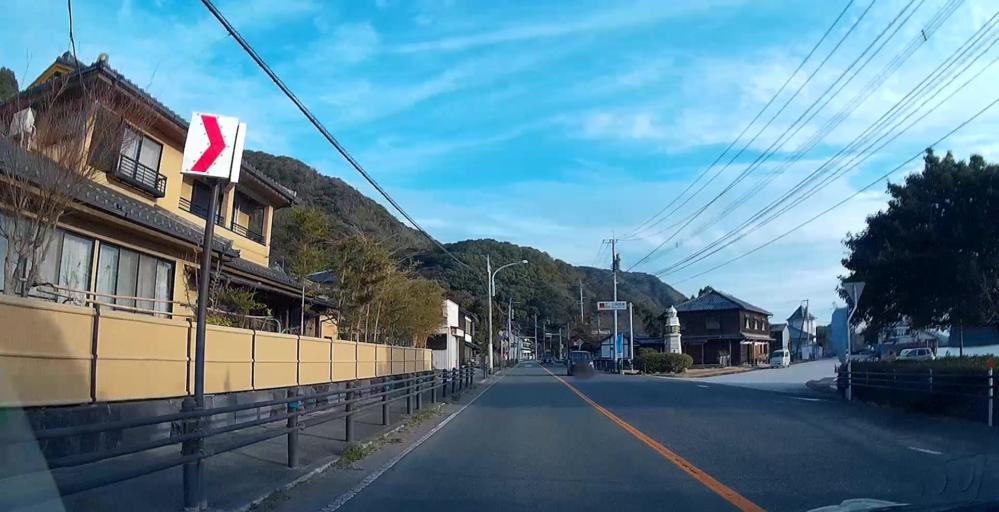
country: JP
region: Nagasaki
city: Shimabara
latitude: 32.6234
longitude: 130.4552
